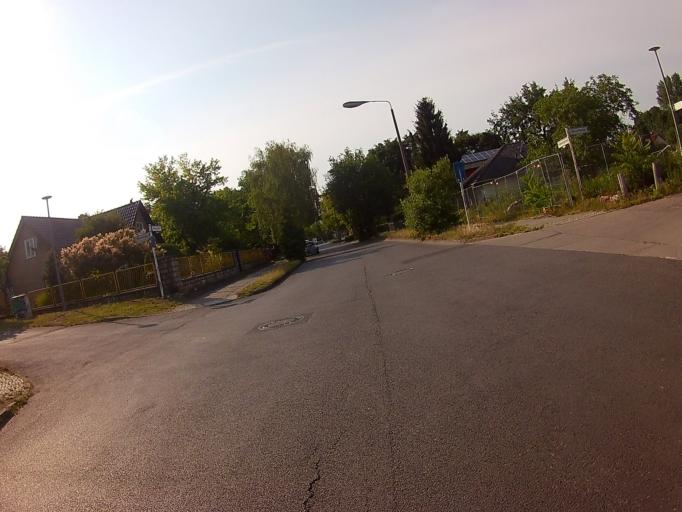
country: DE
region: Berlin
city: Kopenick Bezirk
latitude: 52.4658
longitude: 13.5699
